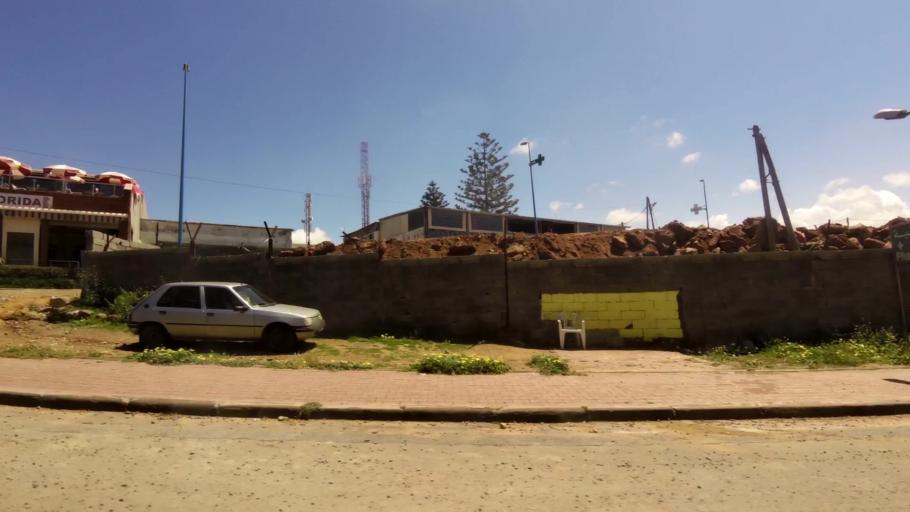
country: MA
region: Grand Casablanca
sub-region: Nouaceur
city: Dar Bouazza
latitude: 33.5306
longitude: -7.8293
